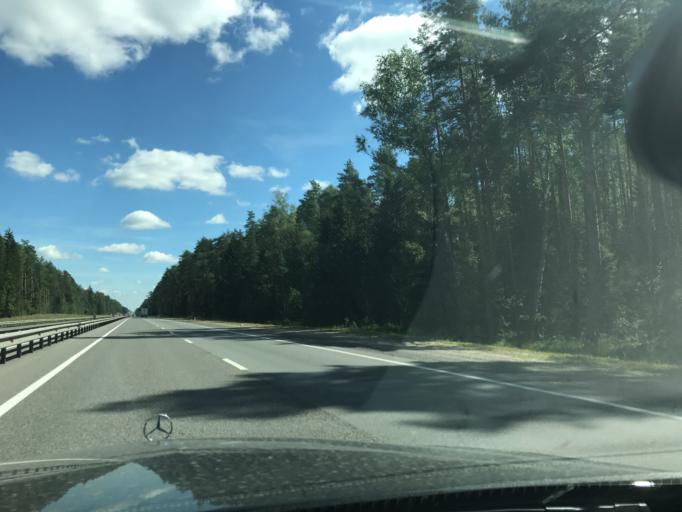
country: RU
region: Vladimir
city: Krasnyy Oktyabr'
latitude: 56.2214
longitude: 41.5274
